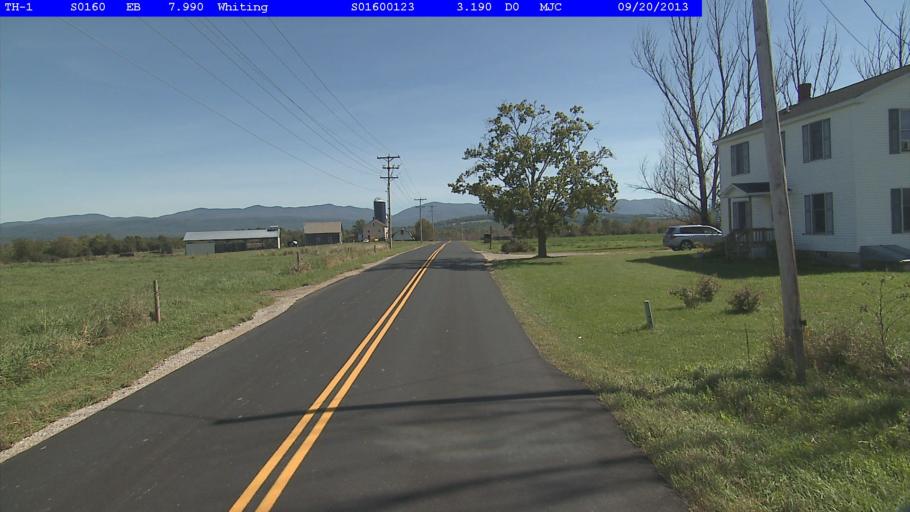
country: US
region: Vermont
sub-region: Rutland County
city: Brandon
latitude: 43.8521
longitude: -73.1669
